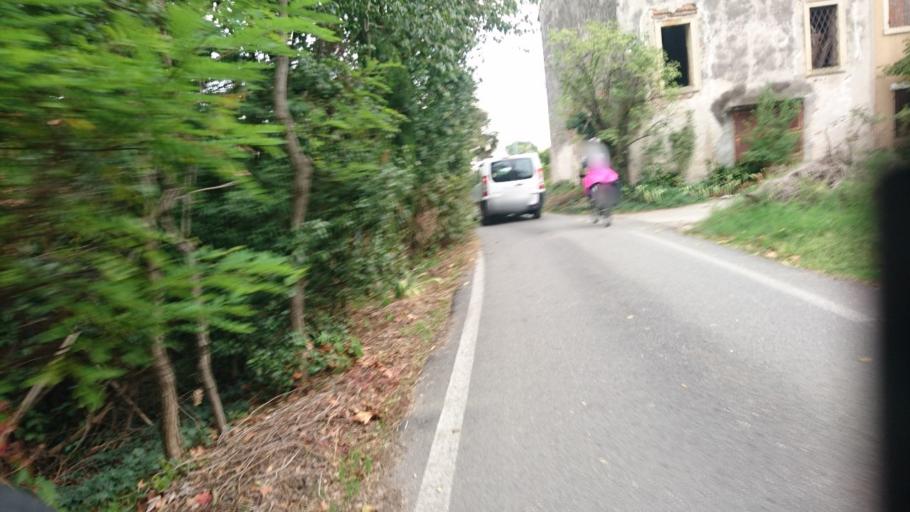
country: IT
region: Veneto
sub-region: Provincia di Verona
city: San Martino Buon Albergo
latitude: 45.4095
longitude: 11.1075
